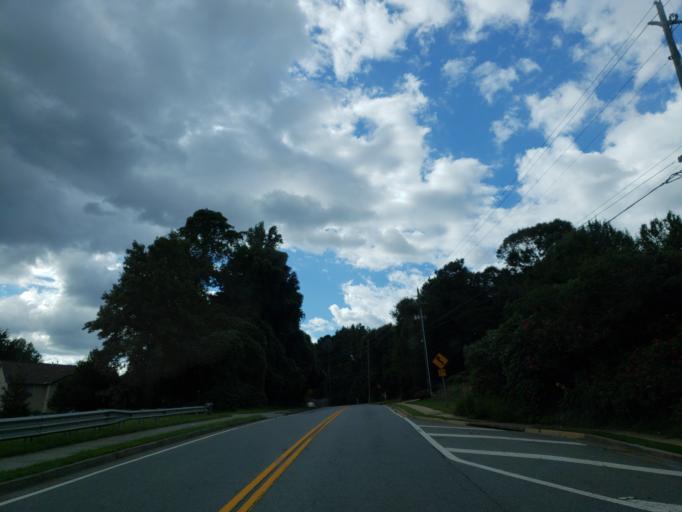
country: US
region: Georgia
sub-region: Cobb County
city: Kennesaw
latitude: 34.0569
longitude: -84.5813
